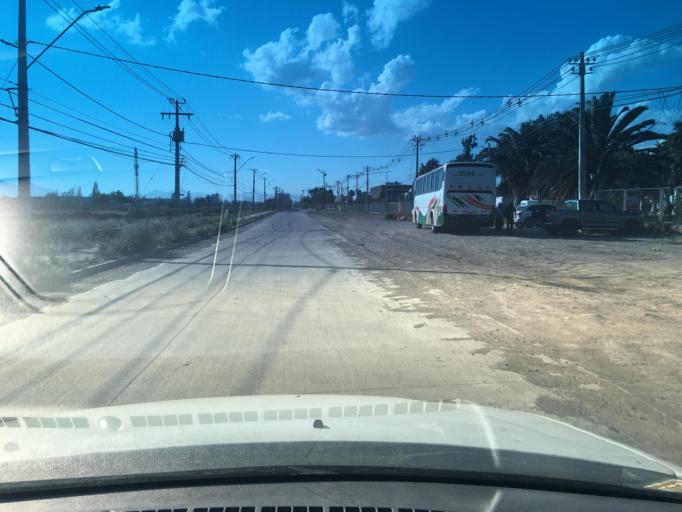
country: CL
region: Santiago Metropolitan
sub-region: Provincia de Chacabuco
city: Chicureo Abajo
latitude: -33.3139
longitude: -70.7129
